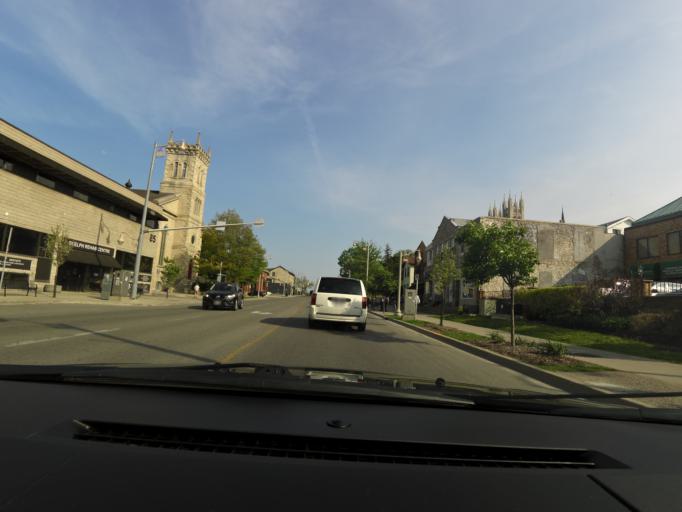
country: CA
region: Ontario
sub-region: Wellington County
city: Guelph
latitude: 43.5449
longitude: -80.2518
